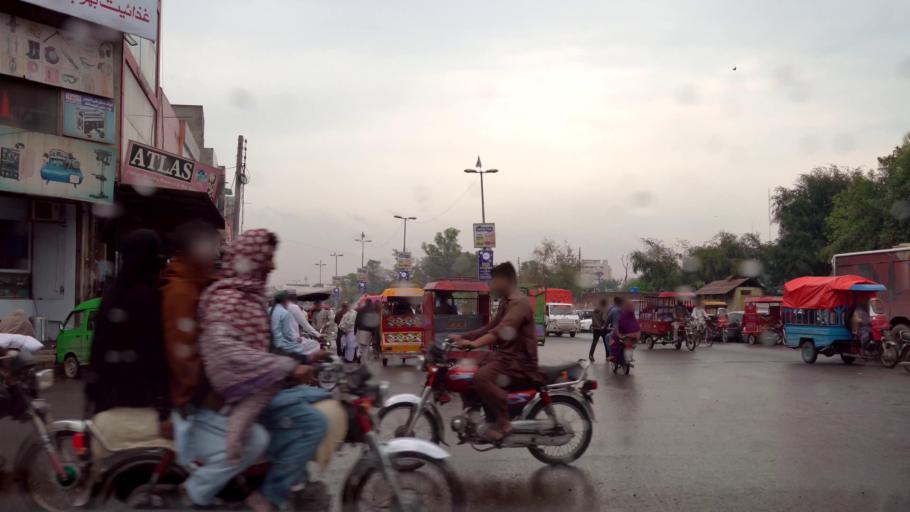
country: PK
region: Punjab
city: Faisalabad
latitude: 31.4190
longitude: 73.0840
